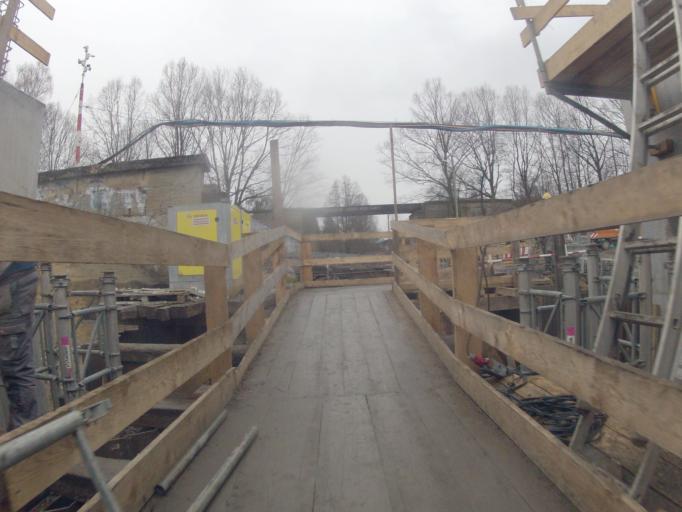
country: PL
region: Lesser Poland Voivodeship
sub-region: Powiat wielicki
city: Czarnochowice
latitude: 50.0180
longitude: 20.0516
